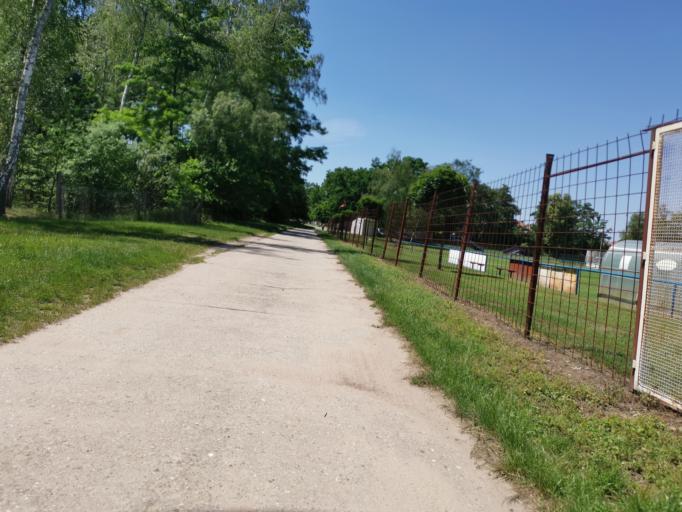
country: CZ
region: South Moravian
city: Vracov
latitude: 48.9685
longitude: 17.2225
